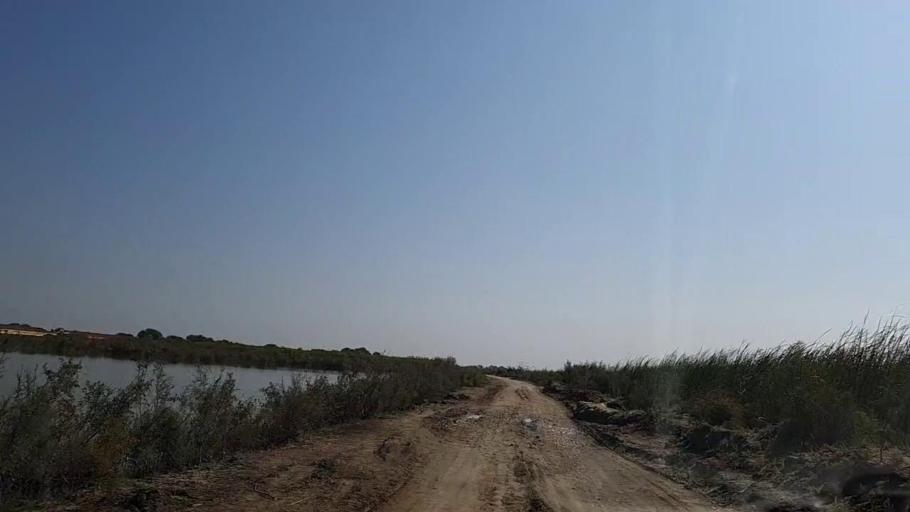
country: PK
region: Sindh
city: Chuhar Jamali
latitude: 24.4638
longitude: 68.1030
